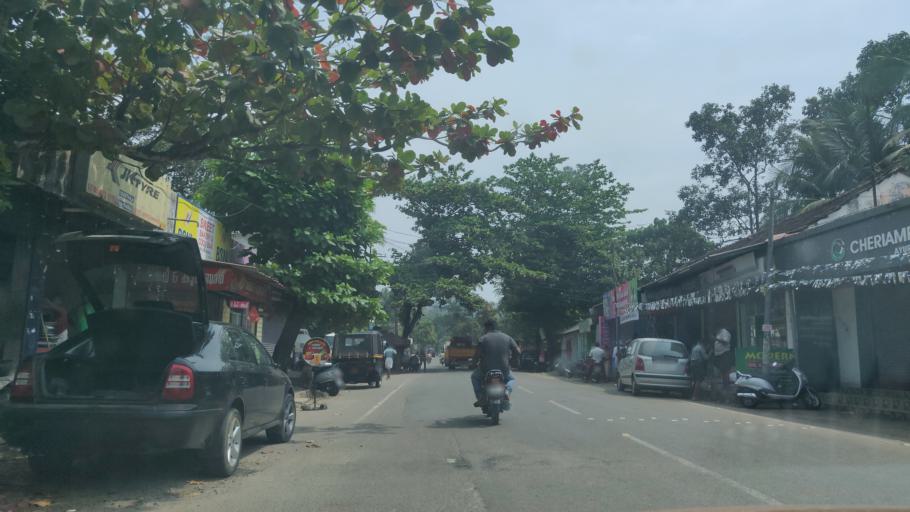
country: IN
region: Kerala
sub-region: Ernakulam
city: Muvattupuzha
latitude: 9.8836
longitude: 76.6449
